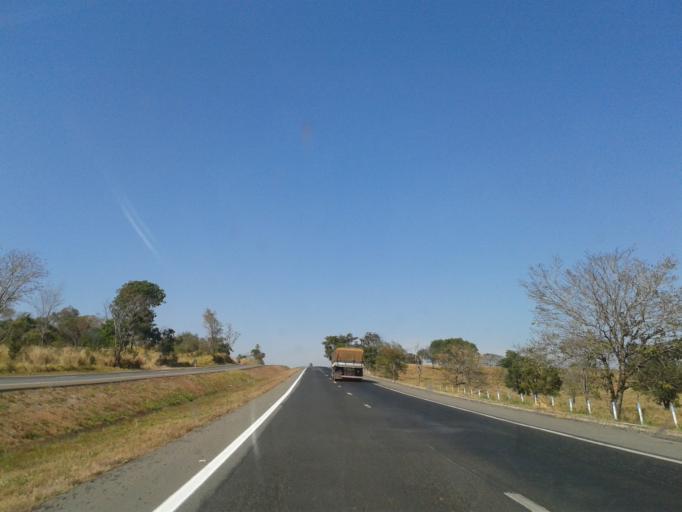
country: BR
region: Goias
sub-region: Piracanjuba
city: Piracanjuba
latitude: -17.3198
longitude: -49.2391
